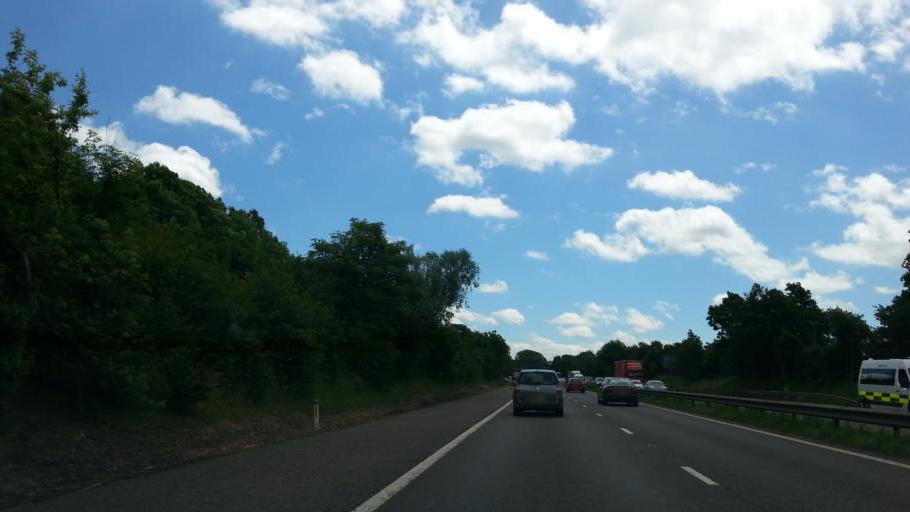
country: GB
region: England
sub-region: Cambridgeshire
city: Grantchester
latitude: 52.1749
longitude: 0.0827
